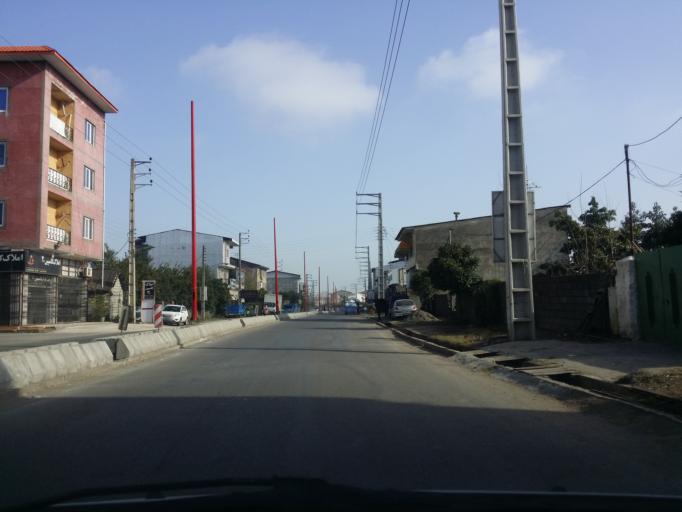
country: IR
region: Mazandaran
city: `Abbasabad
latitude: 36.7110
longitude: 51.1007
